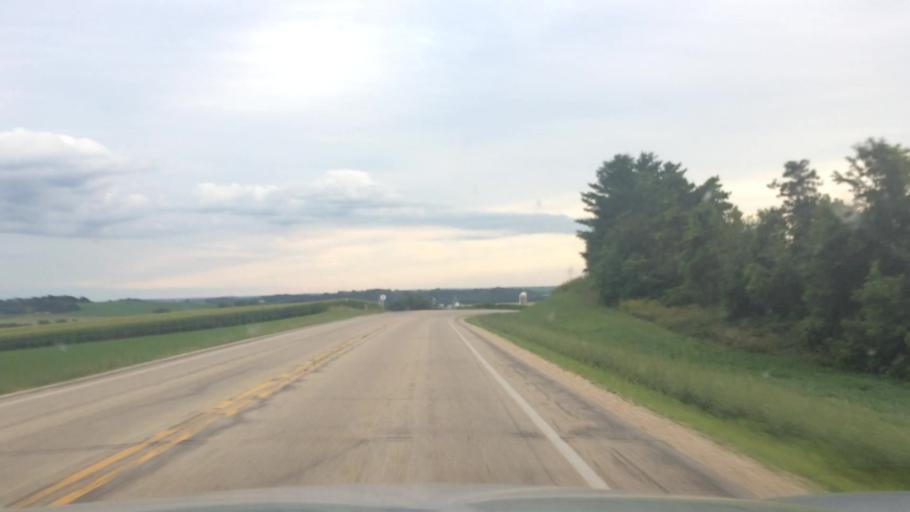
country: US
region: Wisconsin
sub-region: Columbia County
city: Lodi
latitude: 43.2397
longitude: -89.5211
